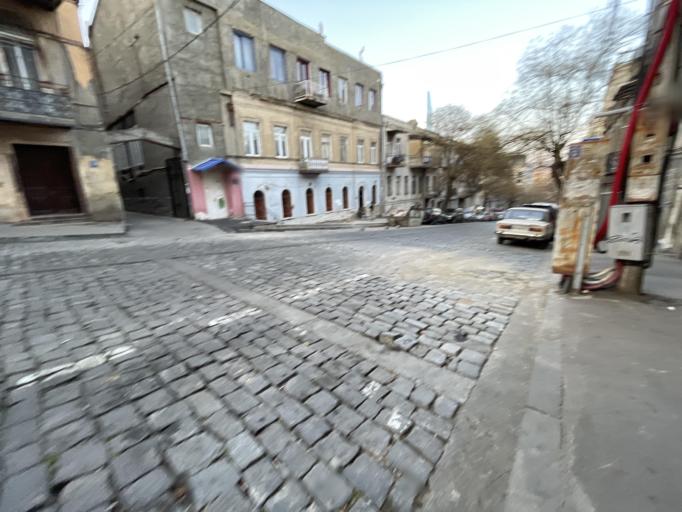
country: GE
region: T'bilisi
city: Tbilisi
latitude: 41.6996
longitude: 44.7929
